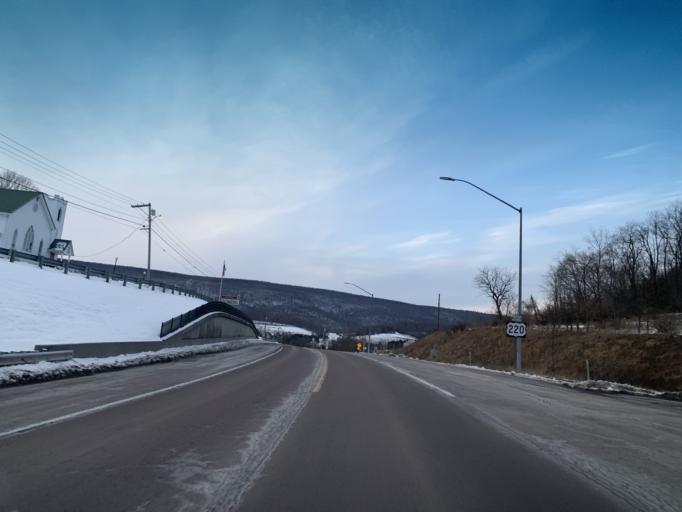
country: US
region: Maryland
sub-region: Allegany County
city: Cumberland
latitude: 39.7216
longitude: -78.7049
